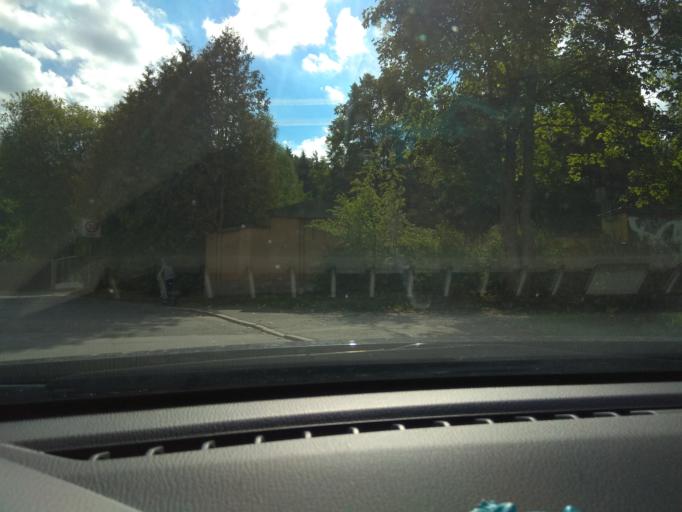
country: DE
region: Saxony
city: Plauen
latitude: 50.4912
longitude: 12.1730
